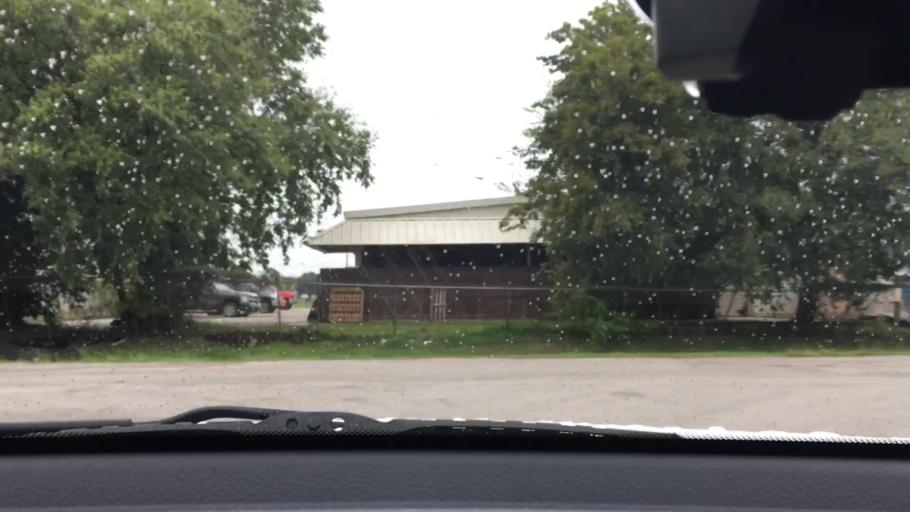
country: US
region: Texas
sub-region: Bexar County
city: Converse
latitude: 29.5121
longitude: -98.3046
